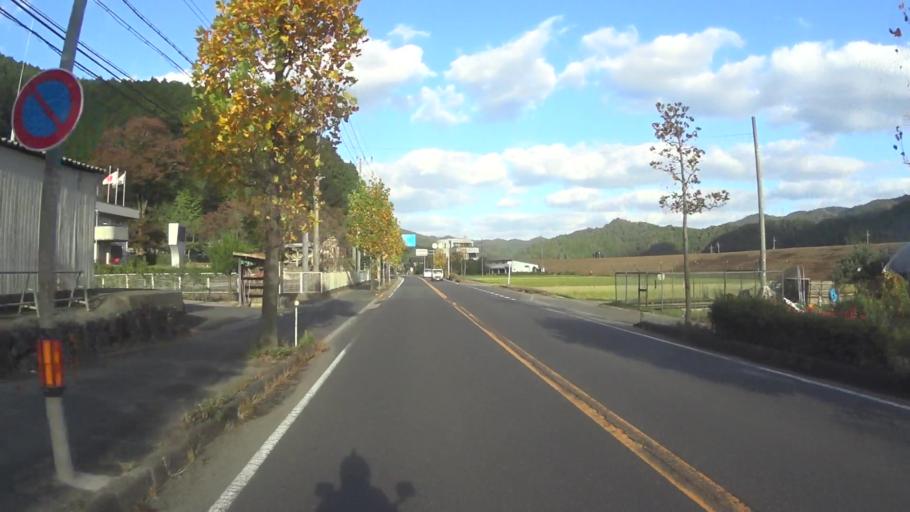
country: JP
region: Kyoto
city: Maizuru
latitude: 35.4286
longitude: 135.2472
